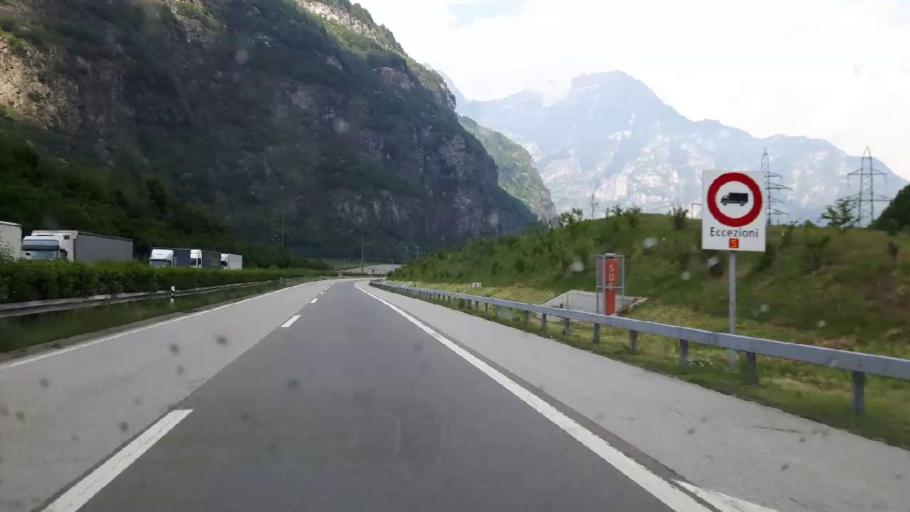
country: CH
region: Ticino
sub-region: Leventina District
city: Bodio
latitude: 46.3743
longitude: 8.9158
